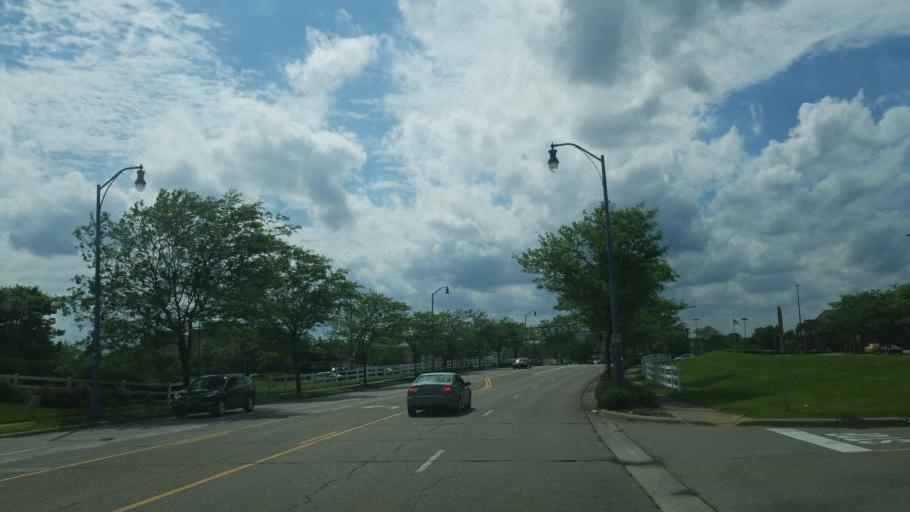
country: US
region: Ohio
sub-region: Franklin County
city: Reynoldsburg
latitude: 39.9366
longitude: -82.7858
